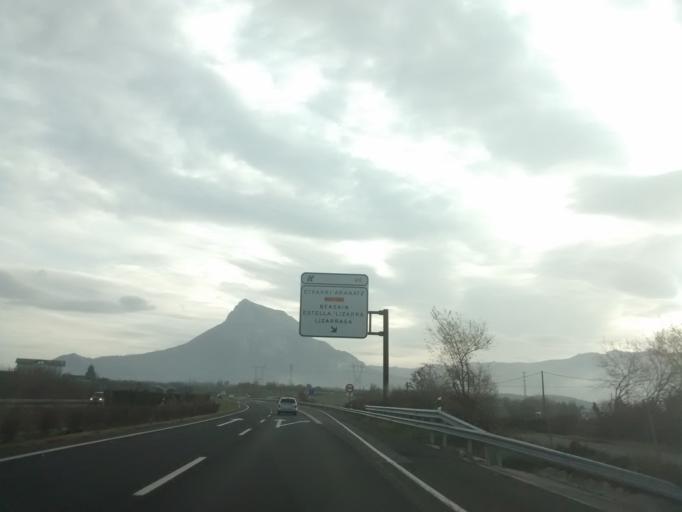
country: ES
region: Navarre
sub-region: Provincia de Navarra
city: Echarri-Aranaz
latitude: 42.8994
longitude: -2.0649
